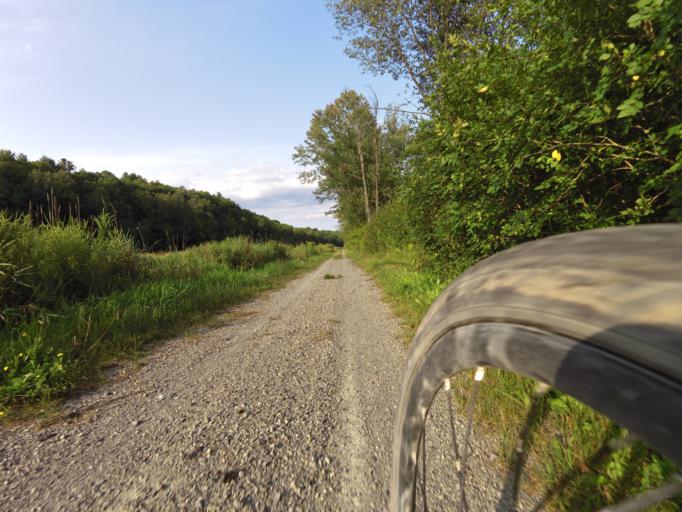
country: CA
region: Ontario
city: Kingston
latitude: 44.5034
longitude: -76.4367
